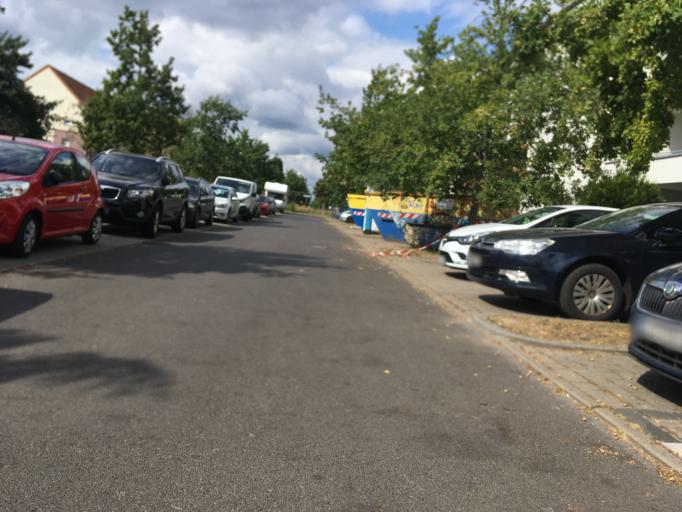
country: DE
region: Berlin
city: Karow
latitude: 52.6125
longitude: 13.4942
